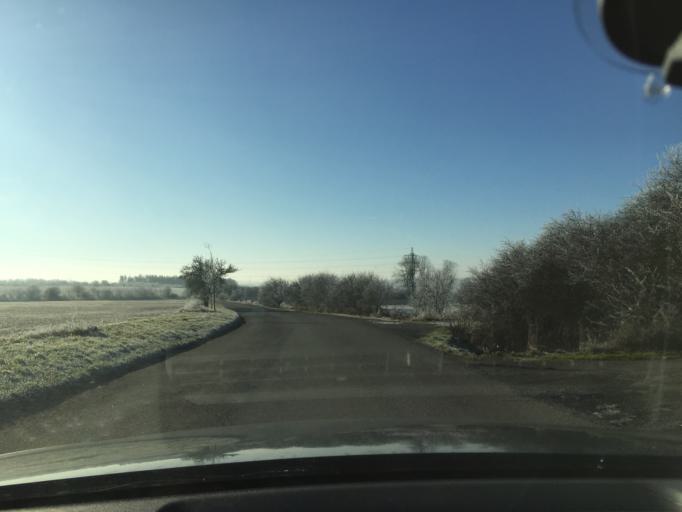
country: CZ
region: Central Bohemia
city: Trebotov
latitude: 50.0095
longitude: 14.2834
